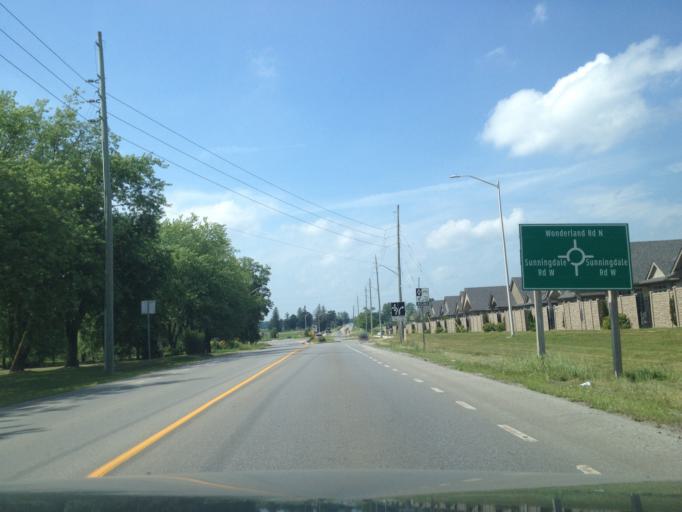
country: CA
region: Ontario
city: London
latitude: 43.0281
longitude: -81.3157
